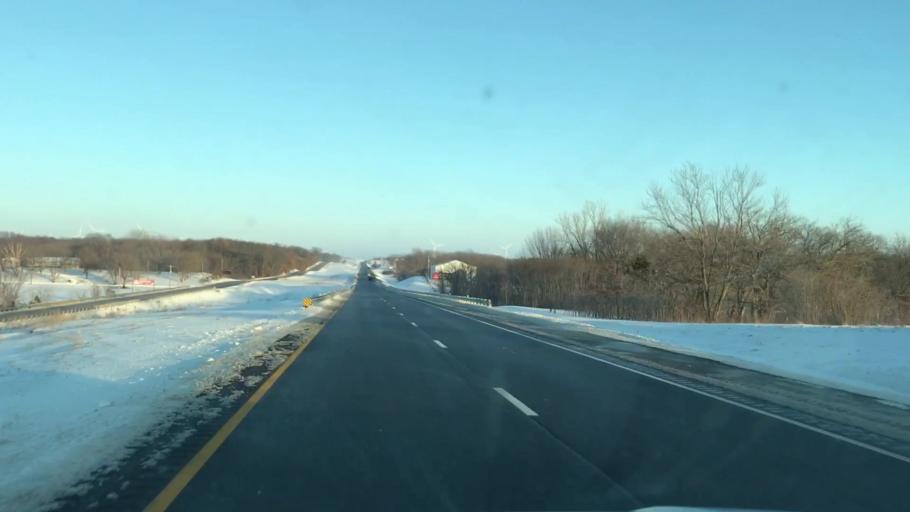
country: US
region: Missouri
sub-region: DeKalb County
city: Maysville
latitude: 39.7620
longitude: -94.4882
